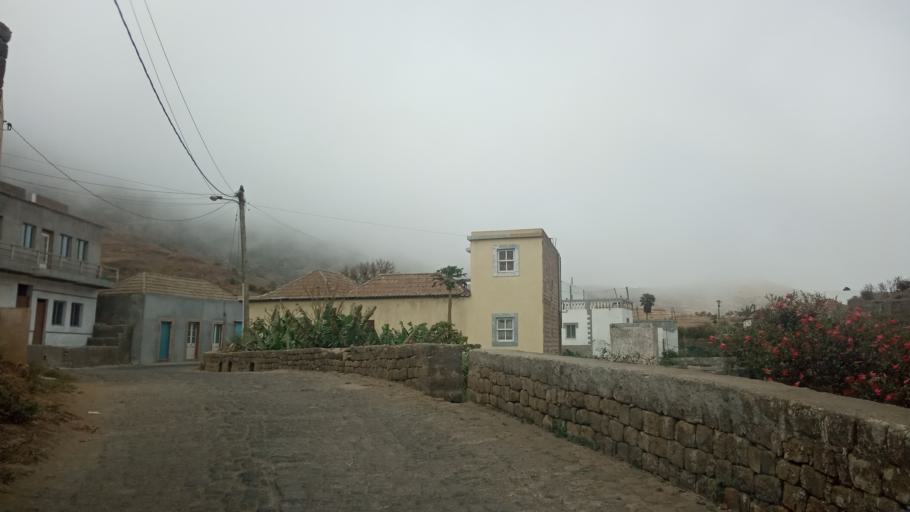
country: CV
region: Brava
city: Vila Nova Sintra
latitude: 14.8710
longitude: -24.7047
